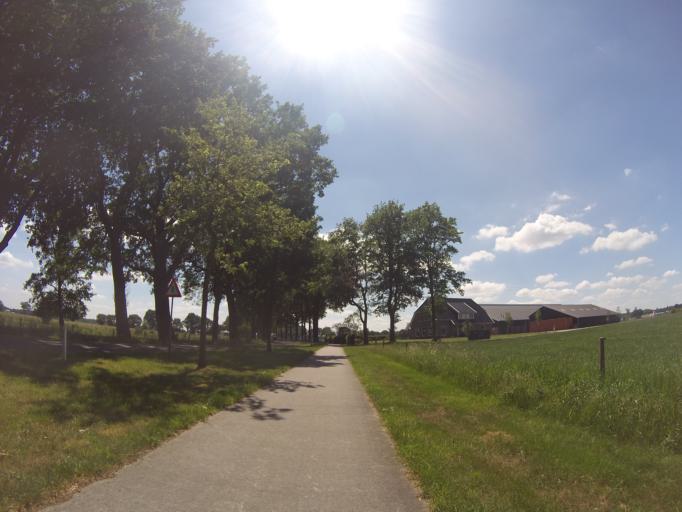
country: NL
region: Drenthe
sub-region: Gemeente Coevorden
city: Sleen
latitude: 52.8462
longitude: 6.8408
